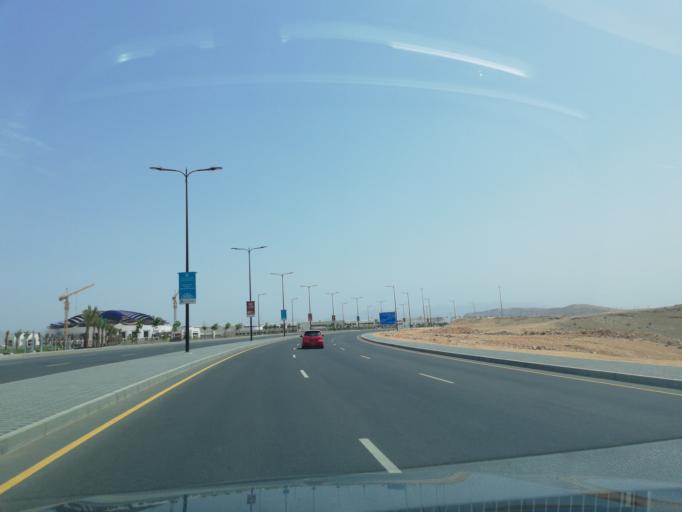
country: OM
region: Muhafazat Masqat
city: Bawshar
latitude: 23.5734
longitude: 58.3253
